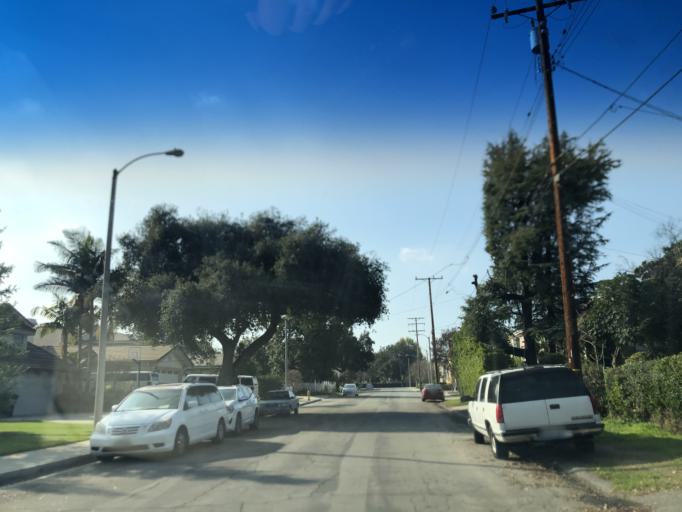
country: US
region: California
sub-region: Los Angeles County
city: East San Gabriel
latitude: 34.1110
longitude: -118.0890
